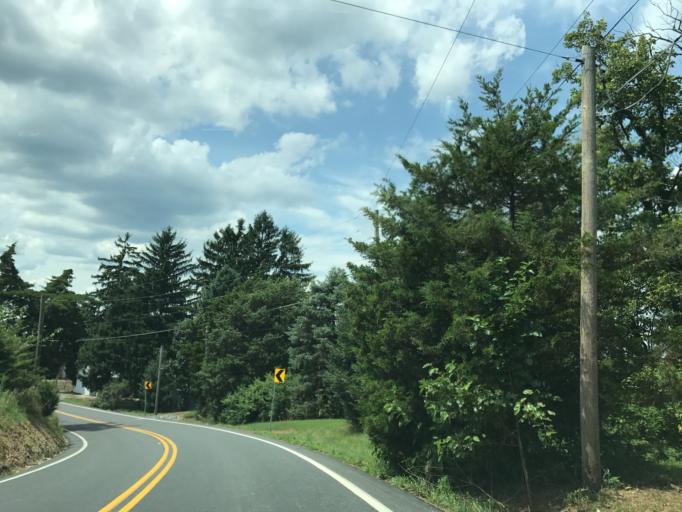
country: US
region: Pennsylvania
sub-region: Lancaster County
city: Mount Joy
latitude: 40.1809
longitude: -76.4798
